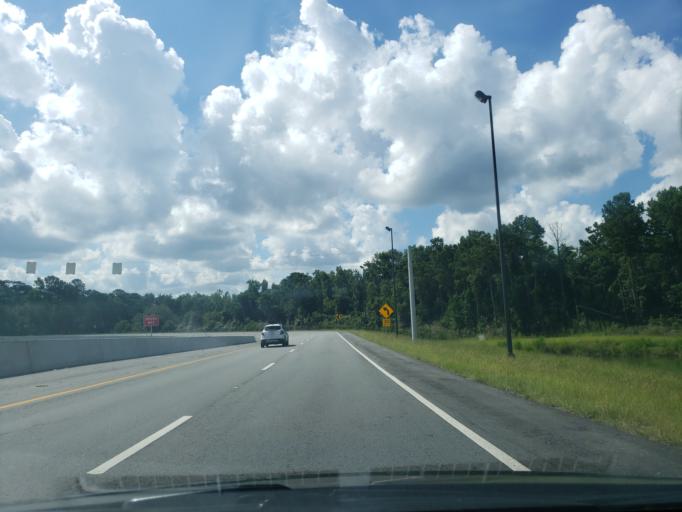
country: US
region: Georgia
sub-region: Chatham County
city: Georgetown
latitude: 31.9850
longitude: -81.2177
